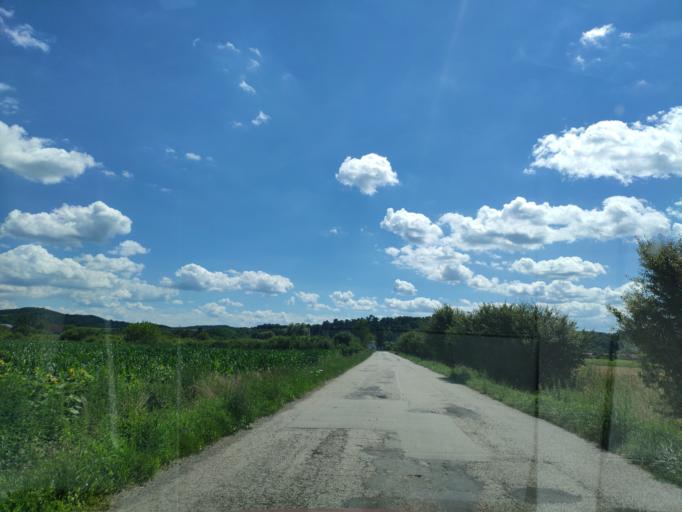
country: HU
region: Borsod-Abauj-Zemplen
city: Arlo
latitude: 48.2848
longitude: 20.1925
